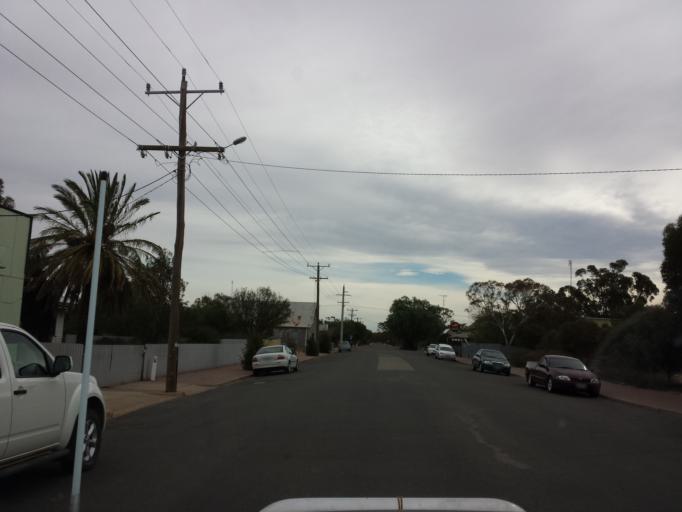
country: AU
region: Victoria
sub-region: Horsham
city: Horsham
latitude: -36.0762
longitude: 142.4153
